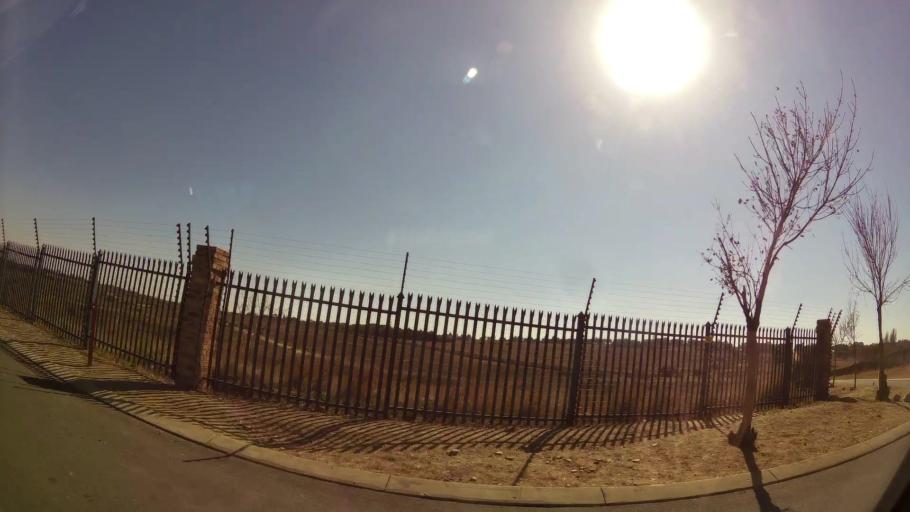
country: ZA
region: Gauteng
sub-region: City of Johannesburg Metropolitan Municipality
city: Midrand
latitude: -25.9505
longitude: 28.0823
